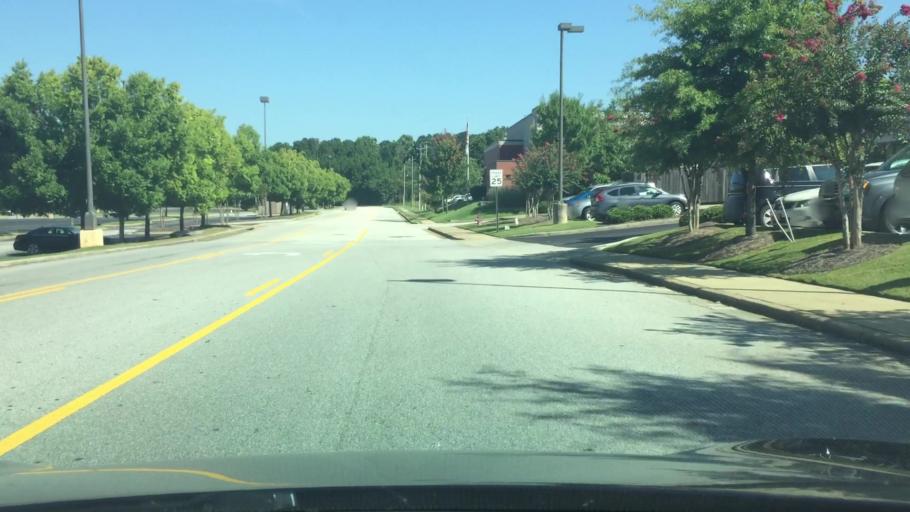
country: US
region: Alabama
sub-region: Lee County
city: Auburn
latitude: 32.6268
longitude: -85.4442
